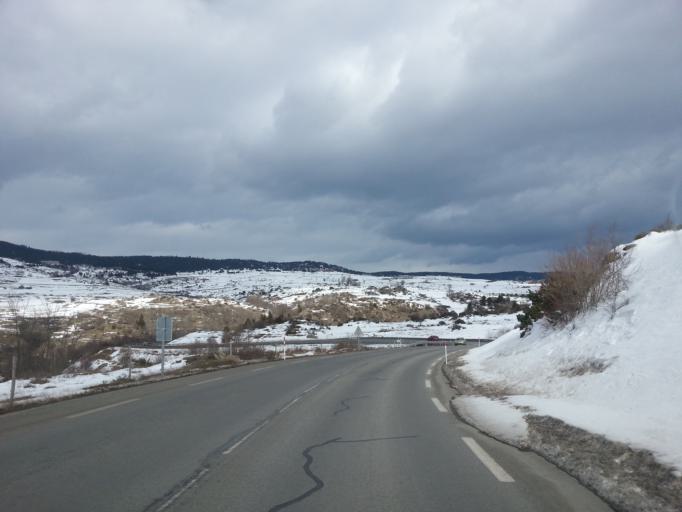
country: ES
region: Catalonia
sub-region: Provincia de Girona
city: Llivia
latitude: 42.4816
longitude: 2.0570
